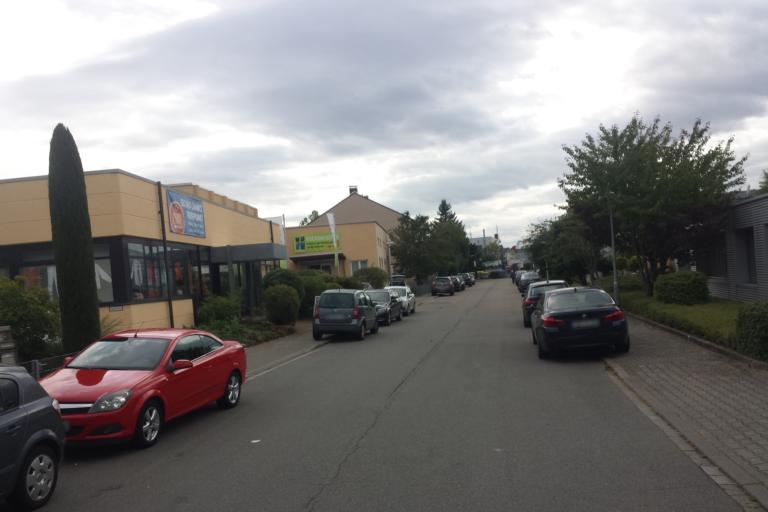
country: DE
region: Baden-Wuerttemberg
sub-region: Karlsruhe Region
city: Mannheim
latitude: 49.5068
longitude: 8.5260
